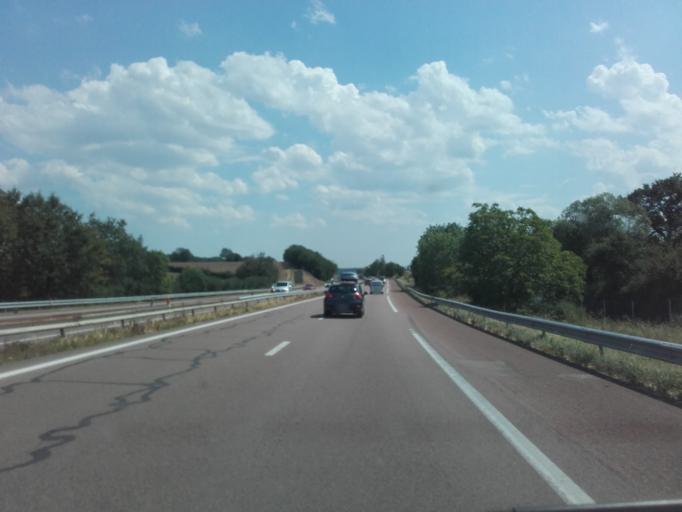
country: FR
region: Bourgogne
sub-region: Departement de l'Yonne
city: Avallon
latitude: 47.5573
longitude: 3.9500
